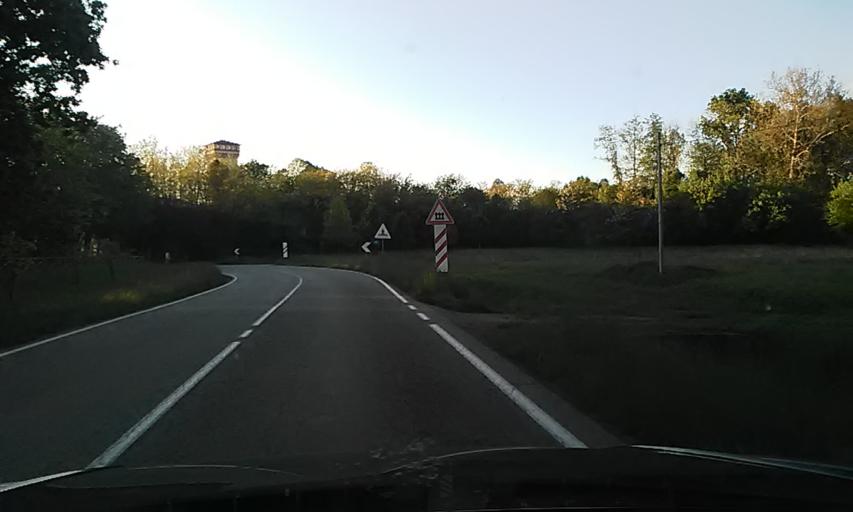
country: IT
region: Piedmont
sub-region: Provincia di Vercelli
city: Rovasenda
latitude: 45.5331
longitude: 8.3147
